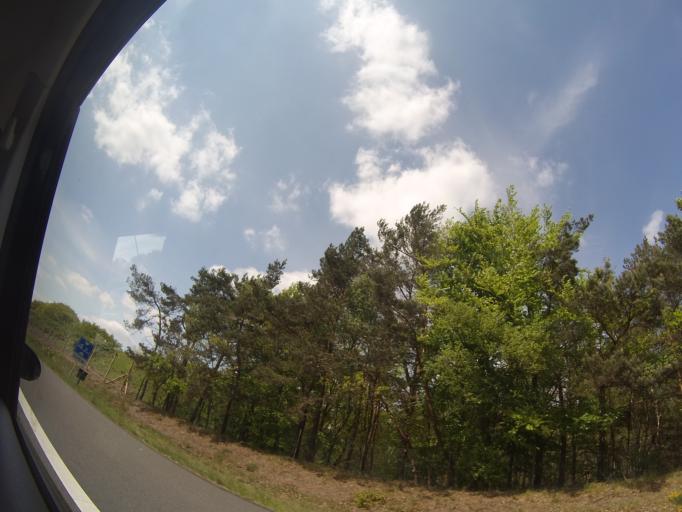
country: NL
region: Utrecht
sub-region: Gemeente Zeist
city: Zeist
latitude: 52.1022
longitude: 5.2161
